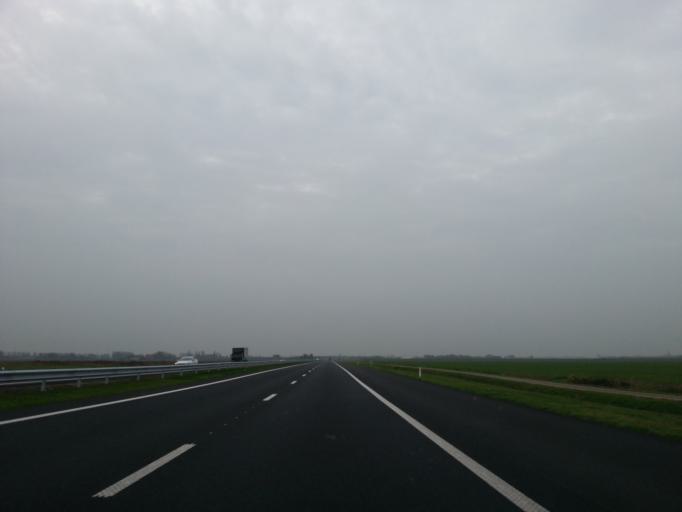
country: NL
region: North Brabant
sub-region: Gemeente Steenbergen
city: Dinteloord
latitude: 51.6140
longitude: 4.3744
